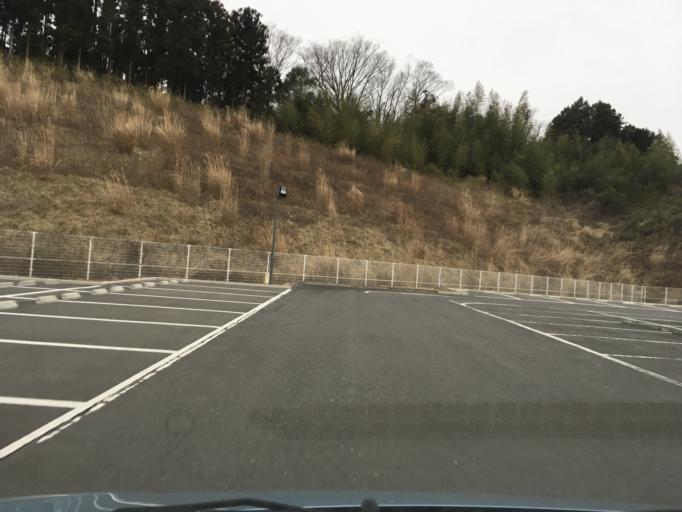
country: JP
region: Miyagi
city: Wakuya
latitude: 38.6986
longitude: 141.1652
